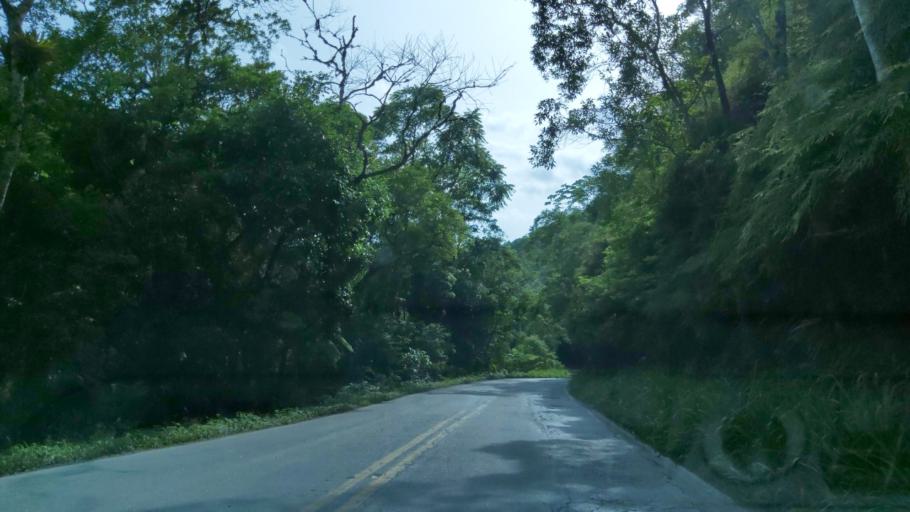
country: BR
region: Sao Paulo
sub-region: Miracatu
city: Miracatu
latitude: -24.0352
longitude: -47.5649
